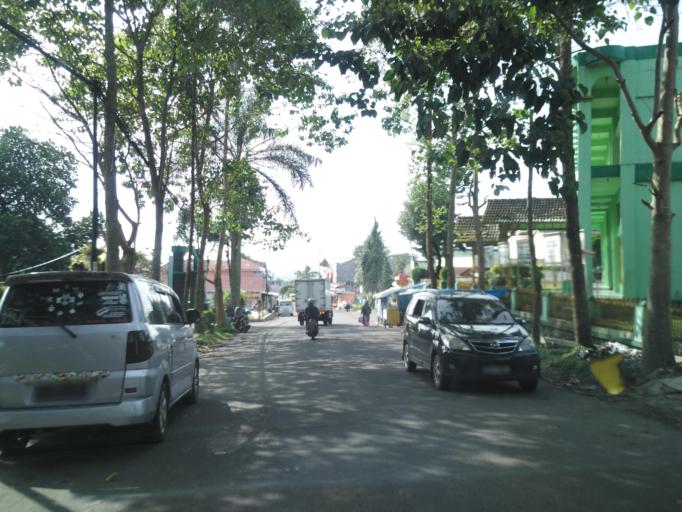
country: ID
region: West Java
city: Sukabumi
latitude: -6.7509
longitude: 107.0478
